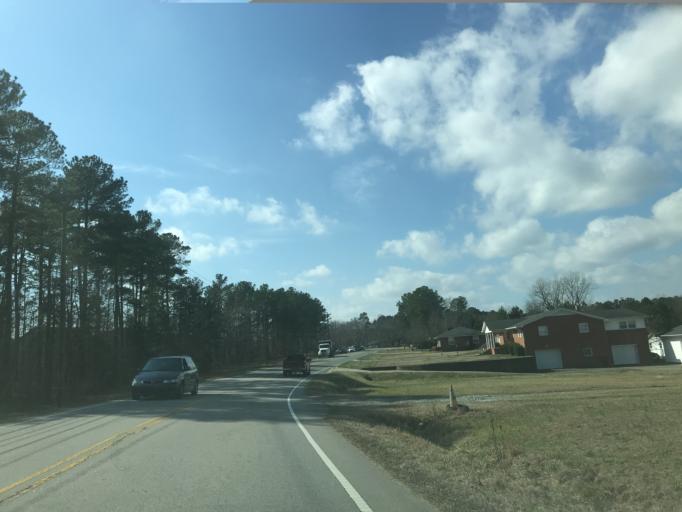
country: US
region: North Carolina
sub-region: Durham County
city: Gorman
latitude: 35.9555
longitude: -78.8271
